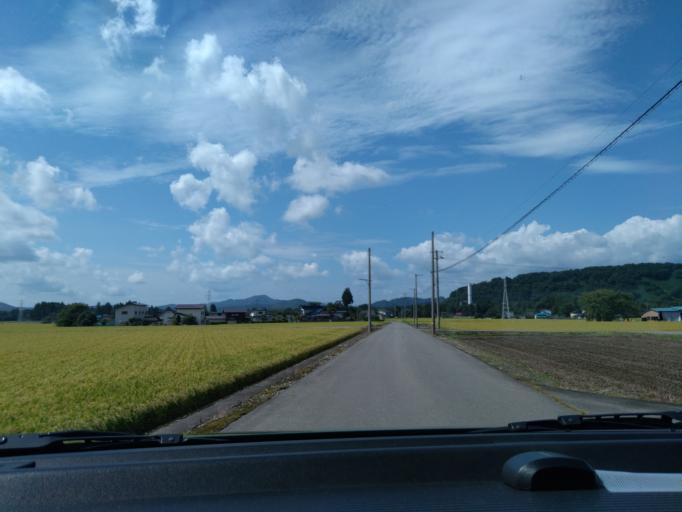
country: JP
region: Akita
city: Kakunodatemachi
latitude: 39.5773
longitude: 140.5902
